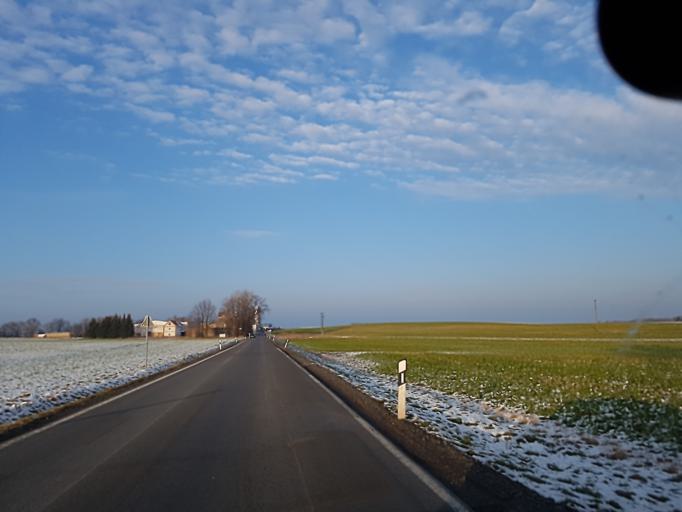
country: DE
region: Saxony
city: Naundorf
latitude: 51.2680
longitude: 13.1146
